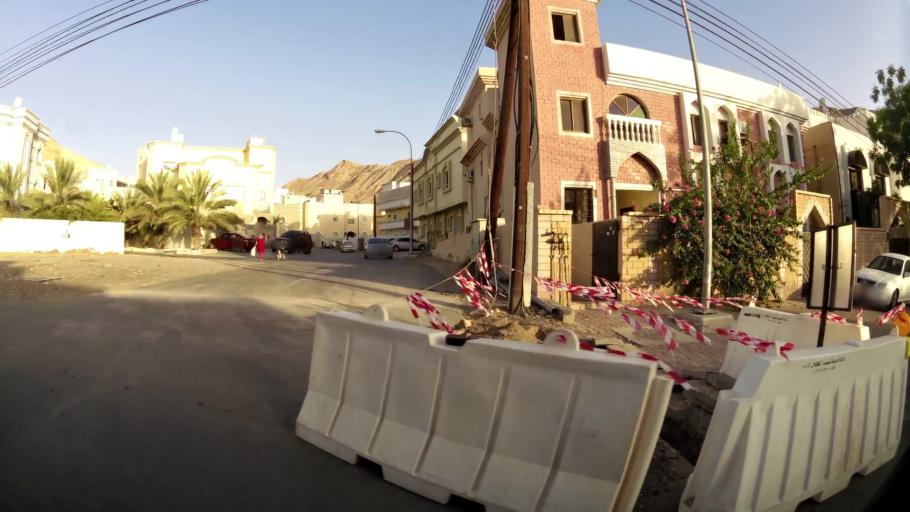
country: OM
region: Muhafazat Masqat
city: Muscat
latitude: 23.5672
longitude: 58.5789
